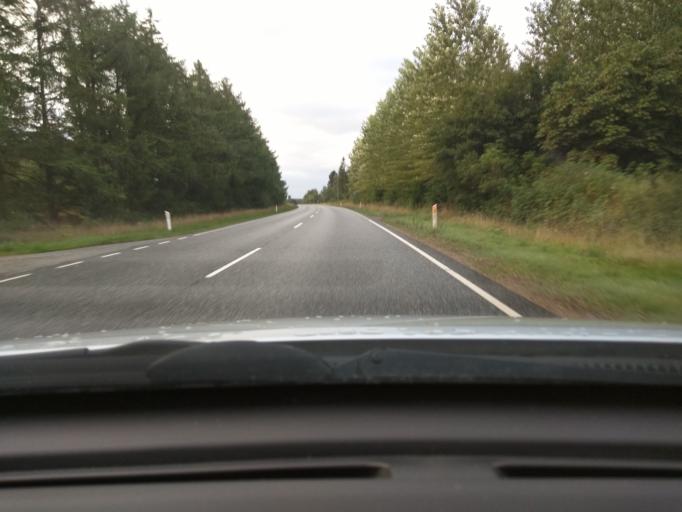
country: DK
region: Central Jutland
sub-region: Ikast-Brande Kommune
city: Bording Kirkeby
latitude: 56.2611
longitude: 9.3151
